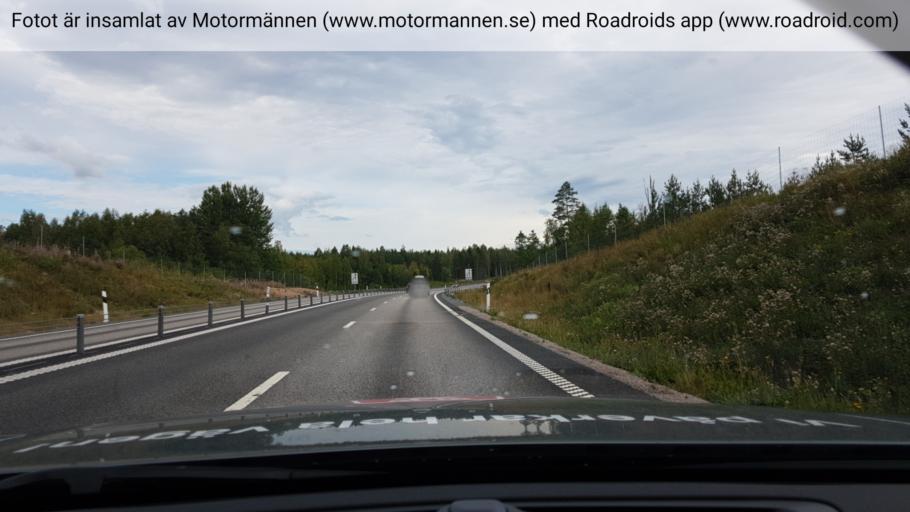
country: SE
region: Uppsala
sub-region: Heby Kommun
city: Tarnsjo
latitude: 60.1275
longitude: 16.9167
